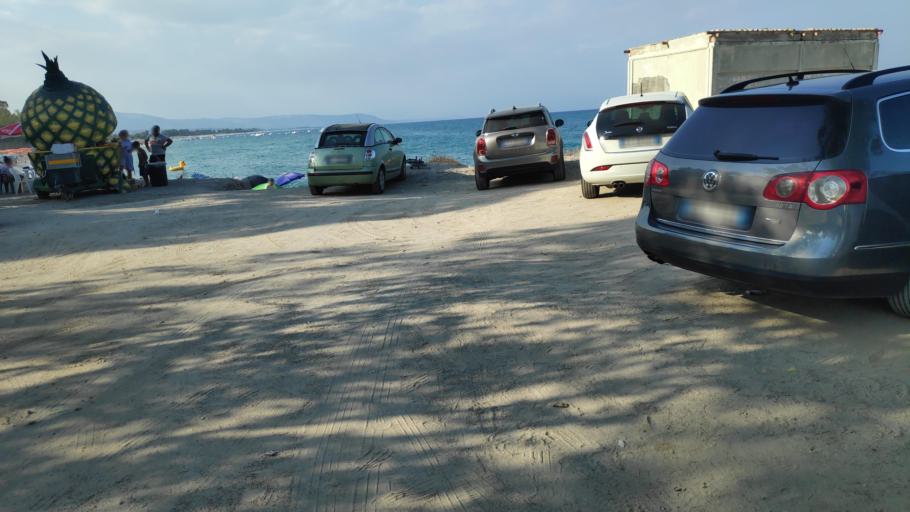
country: IT
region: Calabria
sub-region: Provincia di Catanzaro
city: Isca Marina
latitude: 38.6056
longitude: 16.5657
